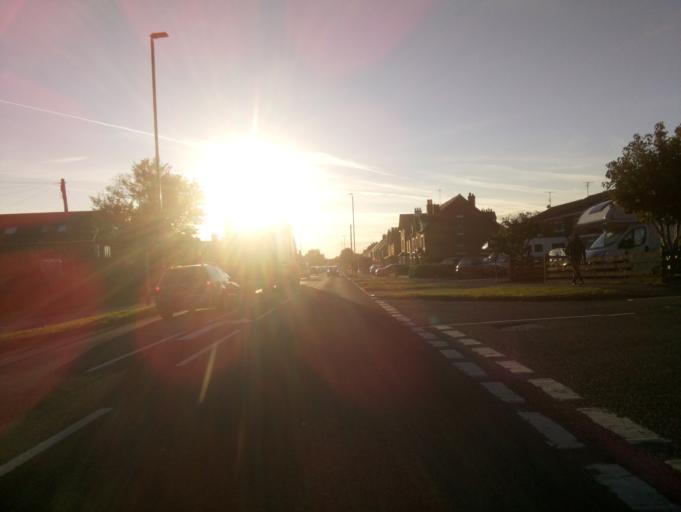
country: GB
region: England
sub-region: Gloucestershire
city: Tewkesbury
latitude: 51.9963
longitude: -2.1358
